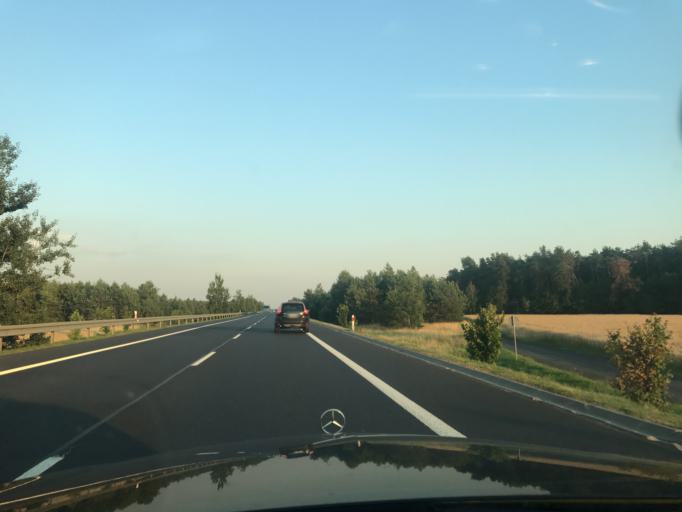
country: PL
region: Lublin Voivodeship
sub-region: Powiat lubartowski
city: Lubartow
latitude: 51.4475
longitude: 22.5825
